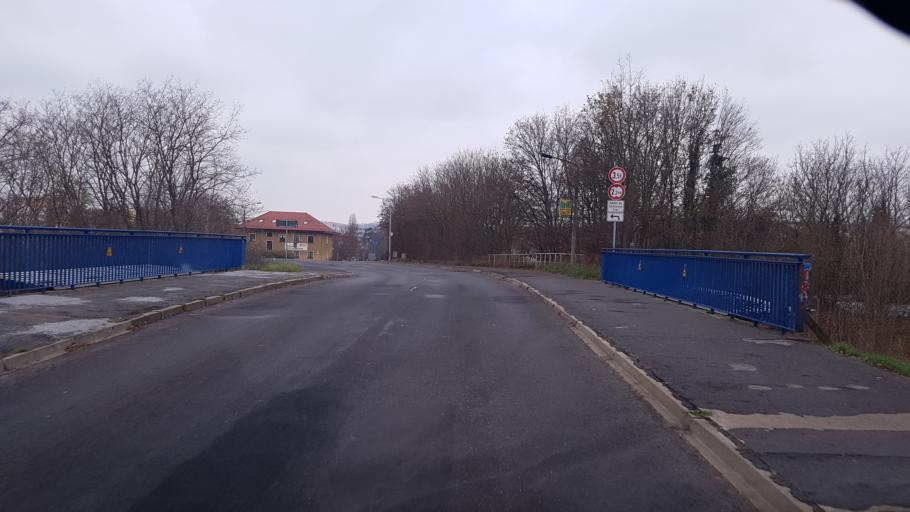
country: DE
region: Brandenburg
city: Eisenhuettenstadt
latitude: 52.1349
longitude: 14.6563
